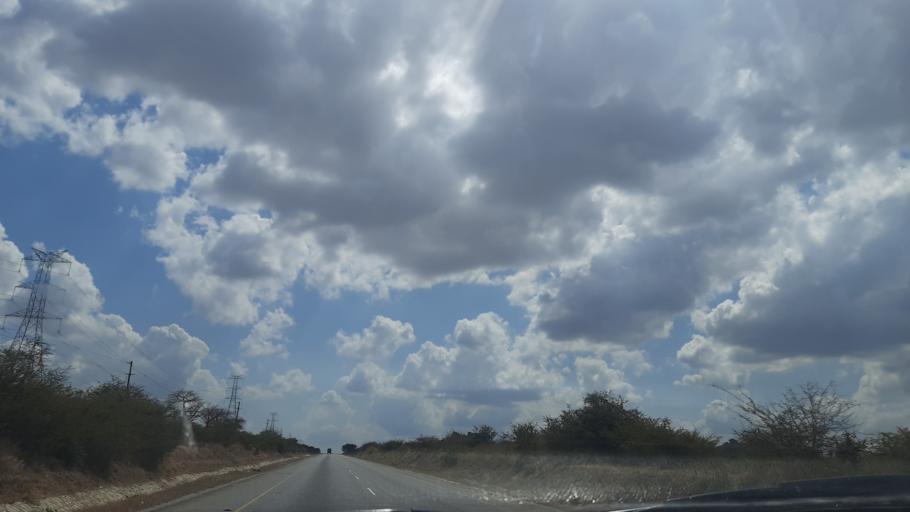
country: TZ
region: Dodoma
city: Dodoma
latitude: -6.0456
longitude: 35.5213
